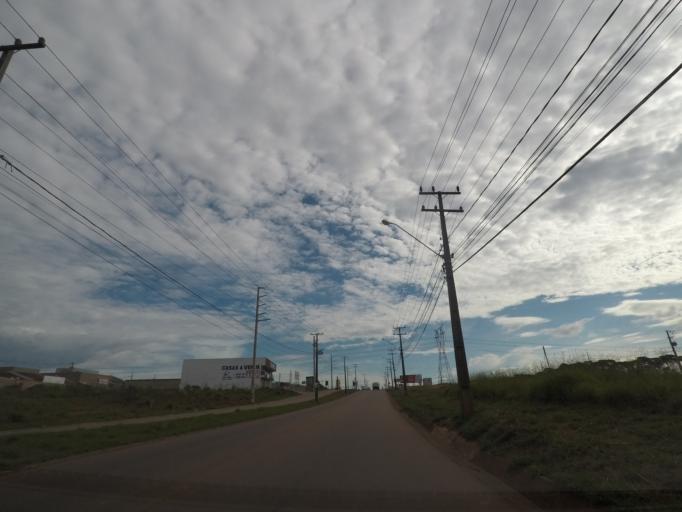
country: BR
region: Parana
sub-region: Araucaria
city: Araucaria
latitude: -25.6350
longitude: -49.2940
